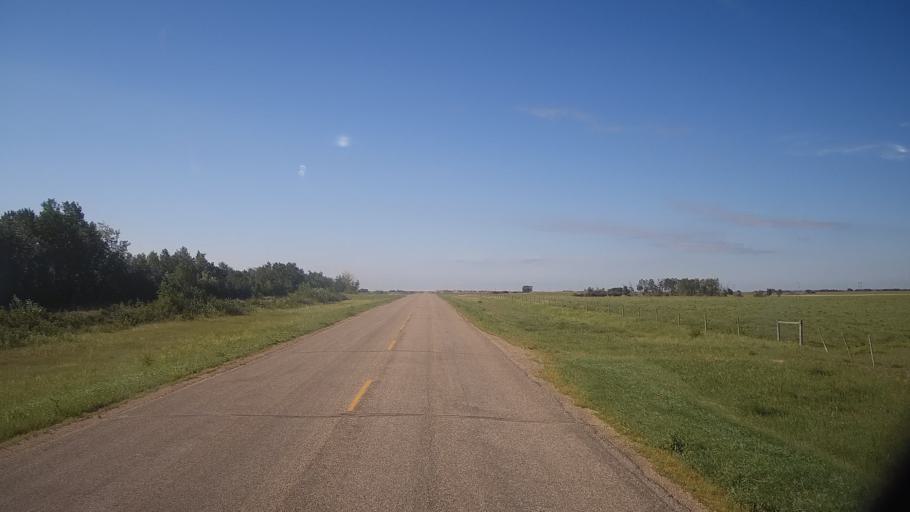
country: CA
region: Saskatchewan
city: Watrous
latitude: 51.7502
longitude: -105.2867
